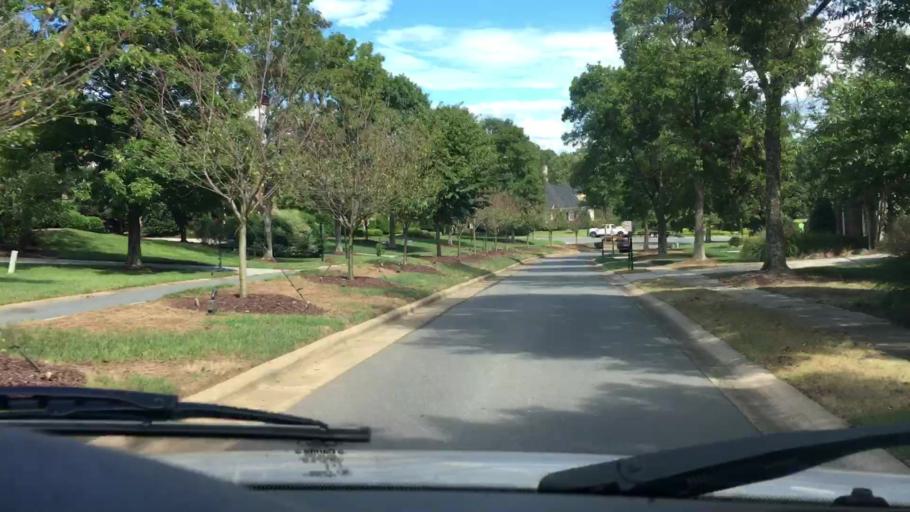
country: US
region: North Carolina
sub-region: Gaston County
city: Davidson
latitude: 35.4648
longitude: -80.8102
